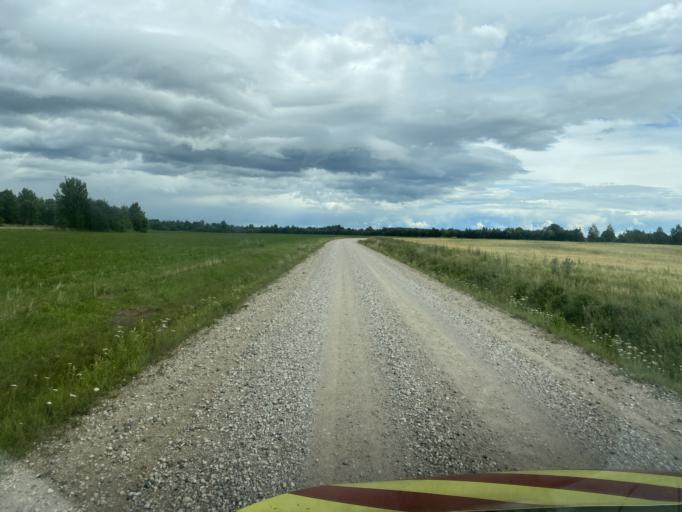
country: EE
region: Valgamaa
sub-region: Torva linn
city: Torva
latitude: 57.9405
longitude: 25.8871
